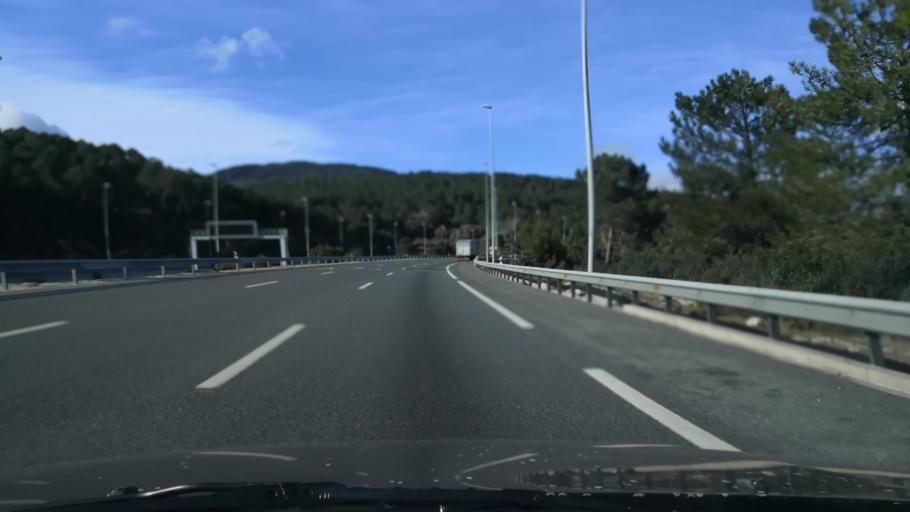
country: ES
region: Madrid
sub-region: Provincia de Madrid
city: Guadarrama
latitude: 40.6774
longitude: -4.1159
